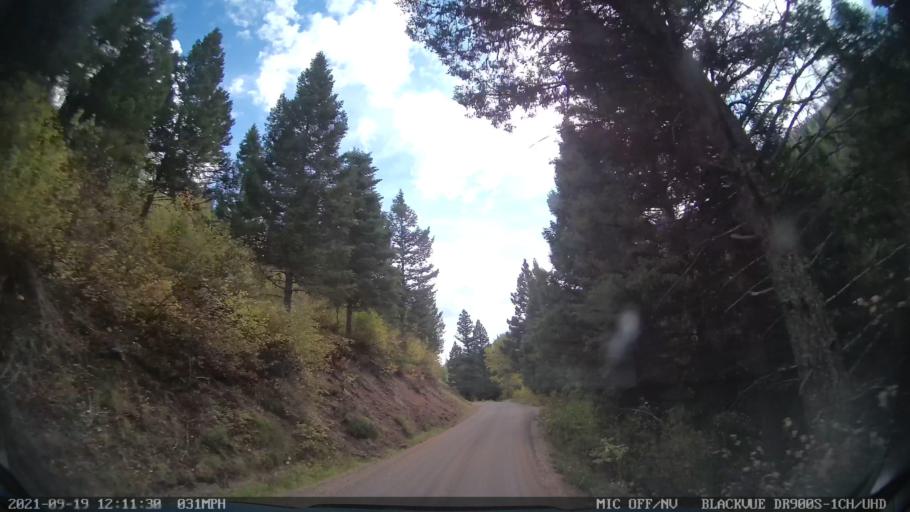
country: US
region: Montana
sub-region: Missoula County
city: Seeley Lake
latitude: 47.1741
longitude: -113.3729
